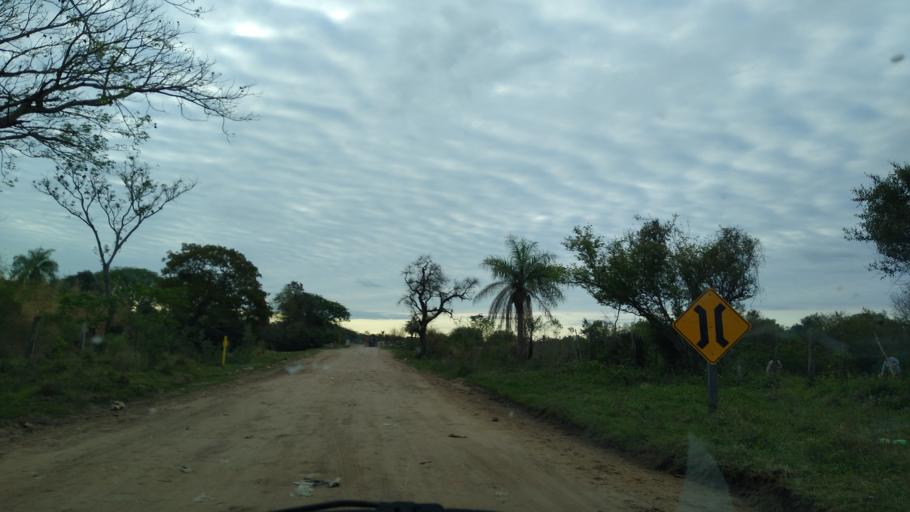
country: AR
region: Chaco
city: Fontana
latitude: -27.3984
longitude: -59.0459
